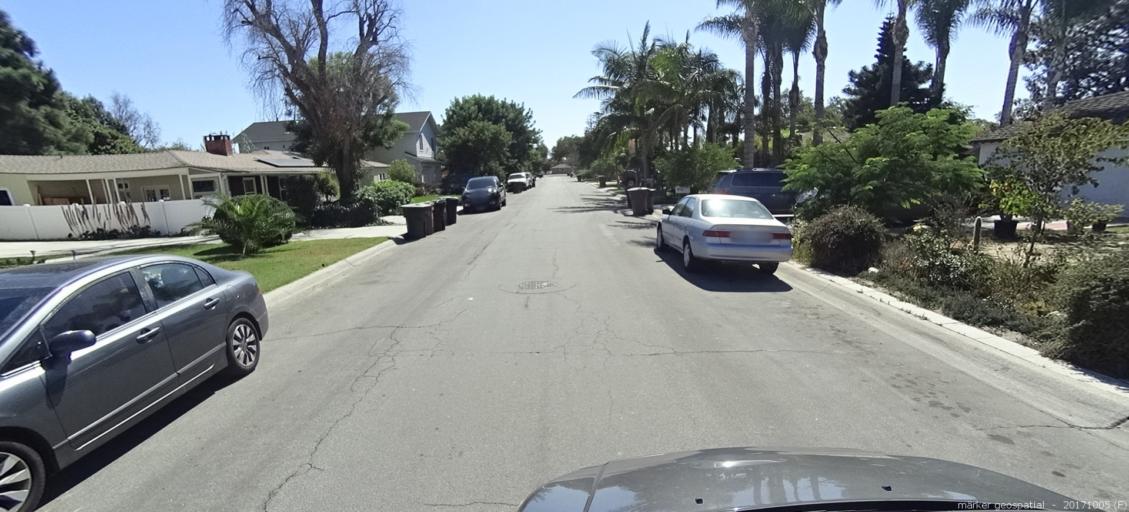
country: US
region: California
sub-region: Orange County
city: Garden Grove
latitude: 33.7834
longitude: -117.9686
